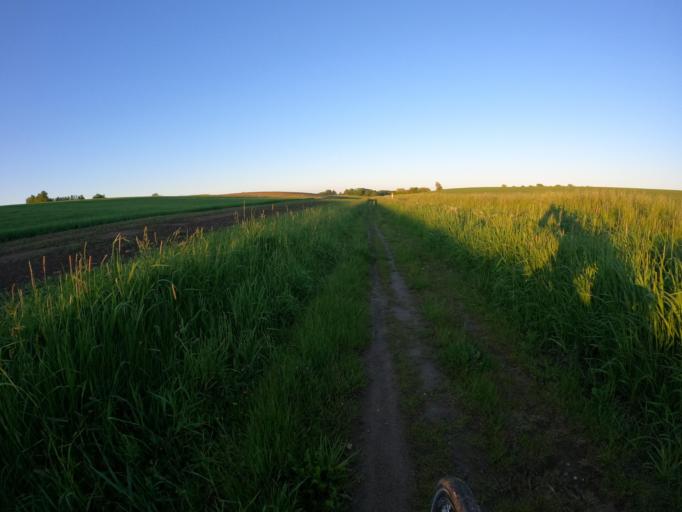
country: DK
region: Zealand
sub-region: Greve Kommune
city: Tune
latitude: 55.6260
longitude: 12.2328
